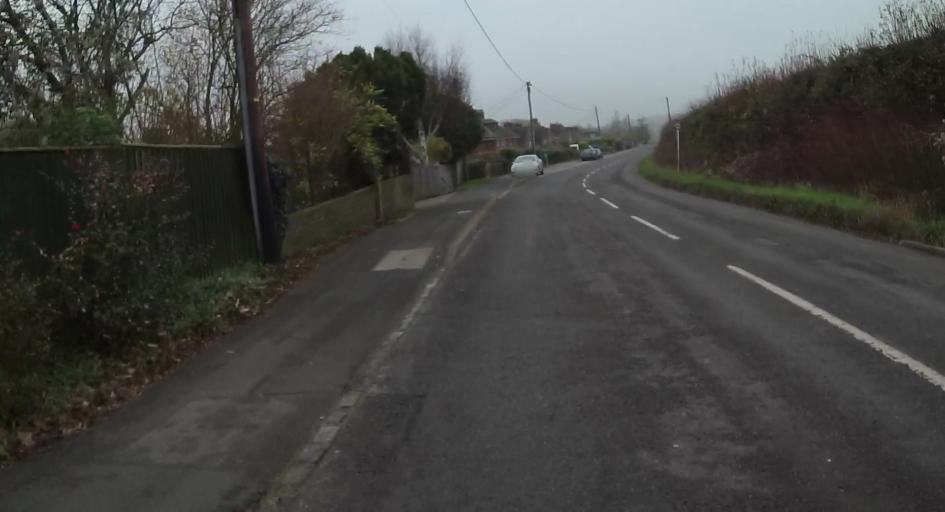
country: GB
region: England
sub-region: Hampshire
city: Kings Worthy
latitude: 51.1003
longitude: -1.2971
